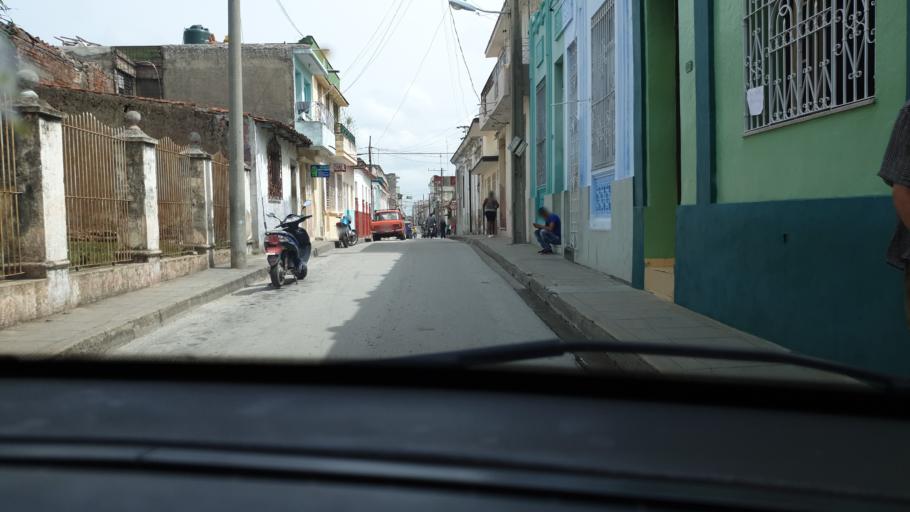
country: CU
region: Villa Clara
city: Santa Clara
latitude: 22.4051
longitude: -79.9665
